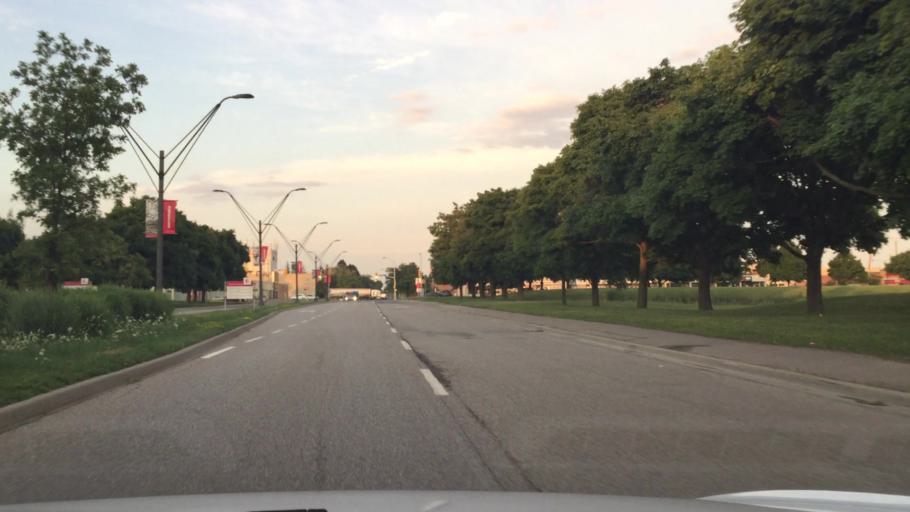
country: CA
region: Ontario
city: Concord
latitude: 43.7746
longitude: -79.4962
